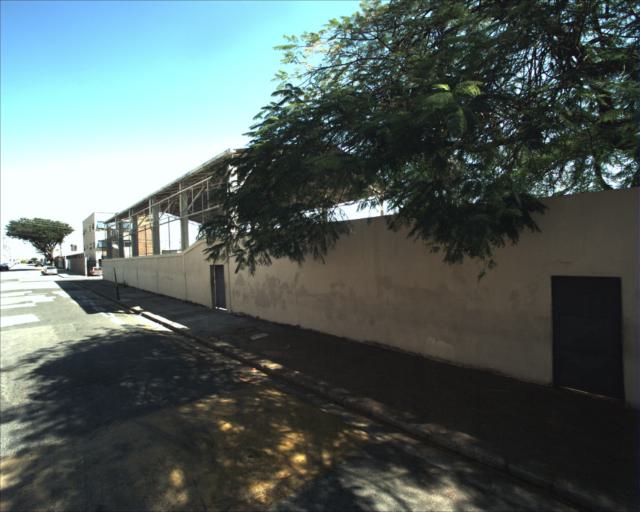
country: BR
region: Sao Paulo
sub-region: Sorocaba
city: Sorocaba
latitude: -23.4935
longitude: -47.4385
